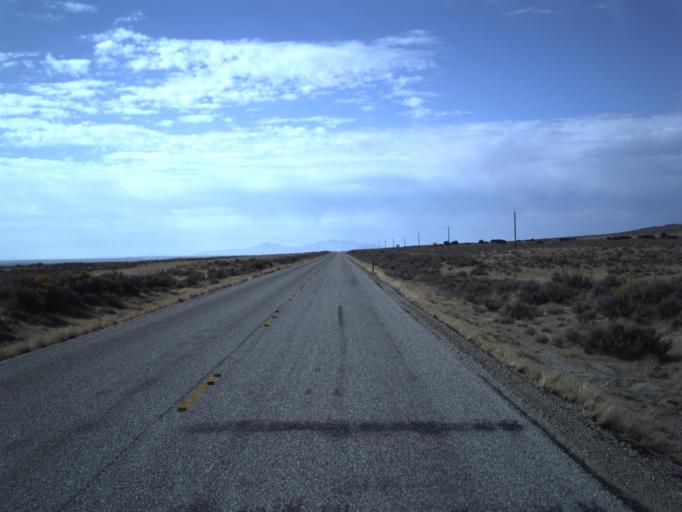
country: US
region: Utah
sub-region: Tooele County
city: Wendover
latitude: 41.5311
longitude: -113.5937
